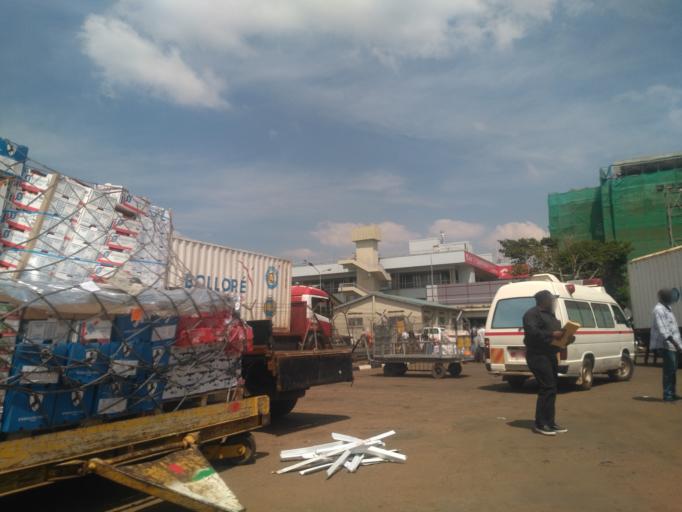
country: UG
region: Central Region
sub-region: Wakiso District
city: Entebbe
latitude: 0.0435
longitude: 32.4434
